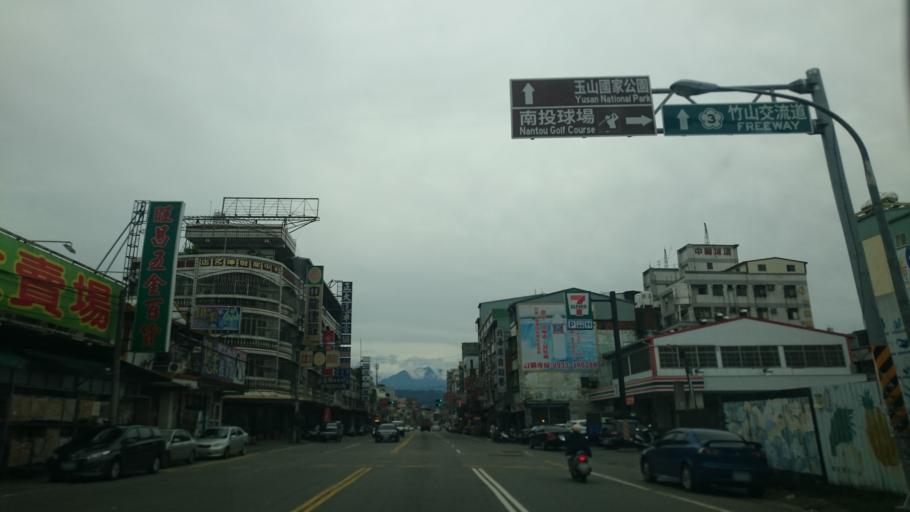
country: TW
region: Taiwan
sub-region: Nantou
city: Nantou
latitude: 23.8405
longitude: 120.7011
